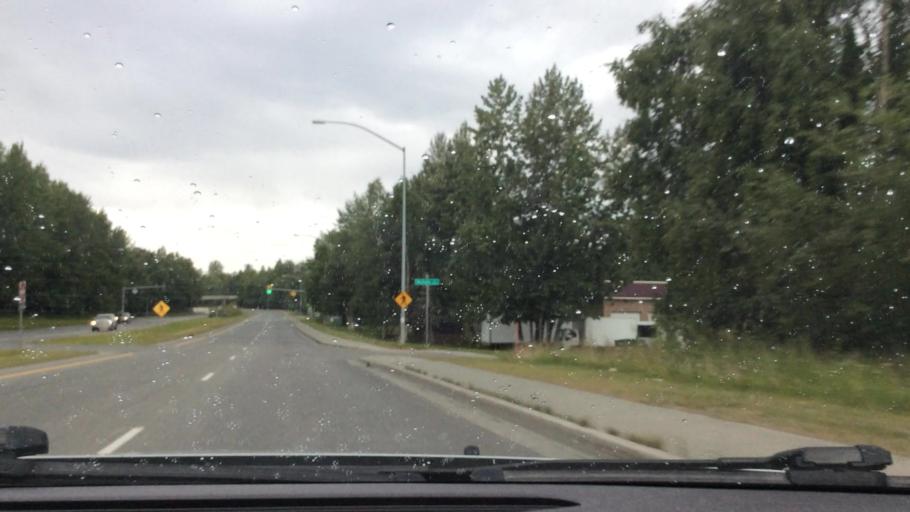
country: US
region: Alaska
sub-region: Anchorage Municipality
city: Anchorage
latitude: 61.1990
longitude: -149.8122
